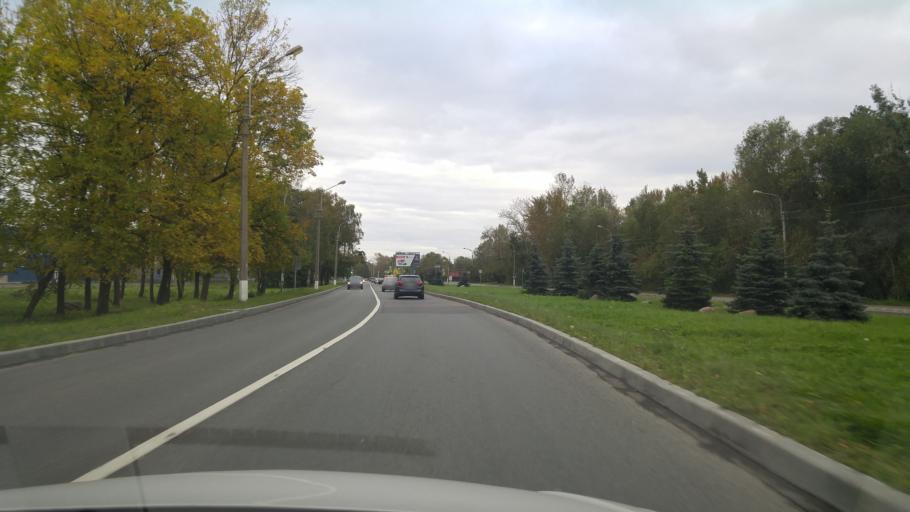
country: RU
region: St.-Petersburg
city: Kronshtadt
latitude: 60.0076
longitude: 29.7377
